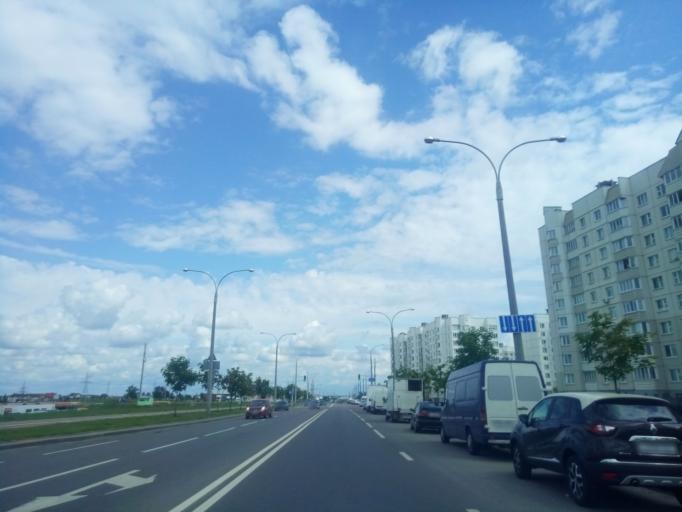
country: BY
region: Minsk
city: Zhdanovichy
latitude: 53.9141
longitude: 27.4148
